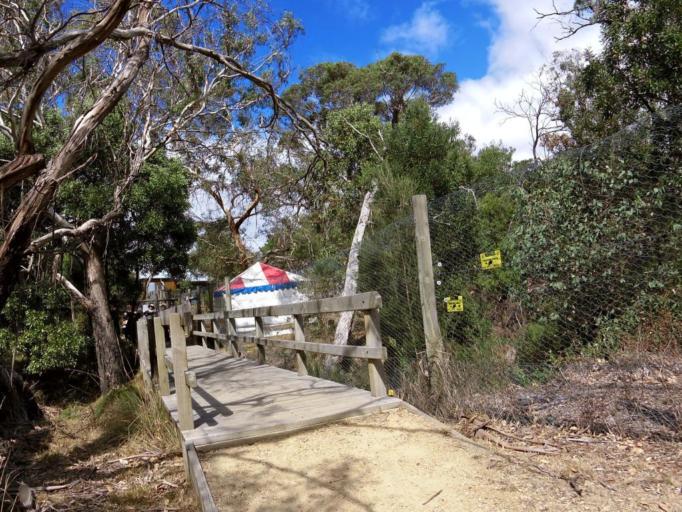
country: AU
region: Victoria
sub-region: Mornington Peninsula
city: Mount Martha
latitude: -38.2677
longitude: 145.0429
